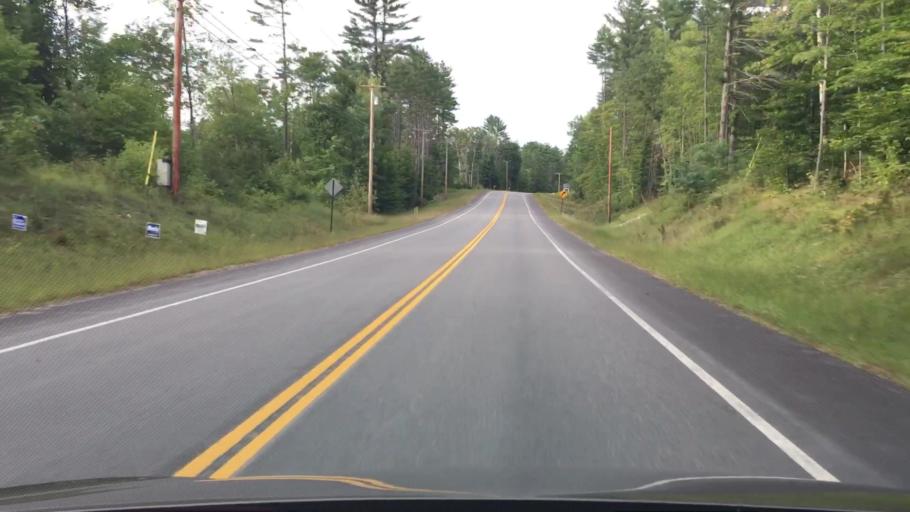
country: US
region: Maine
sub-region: Oxford County
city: Lovell
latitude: 44.0570
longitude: -70.8553
